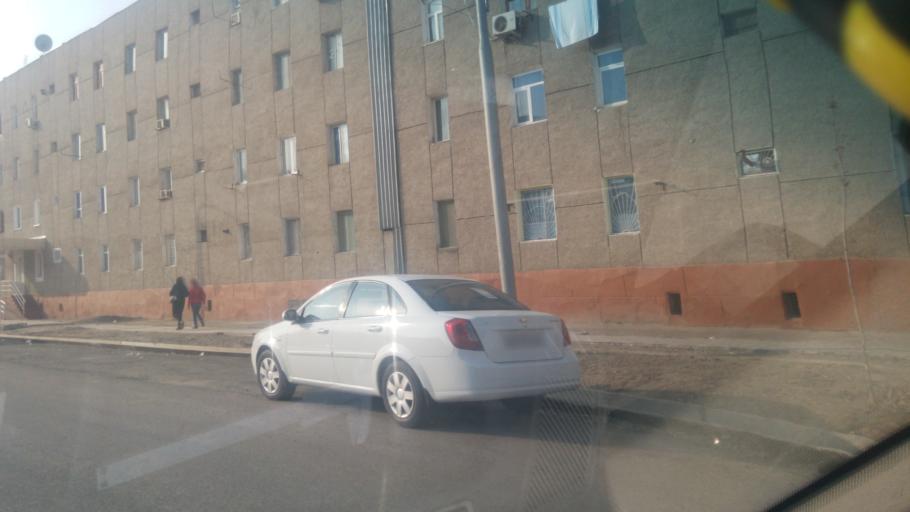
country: UZ
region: Sirdaryo
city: Guliston
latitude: 40.5044
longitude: 68.7745
